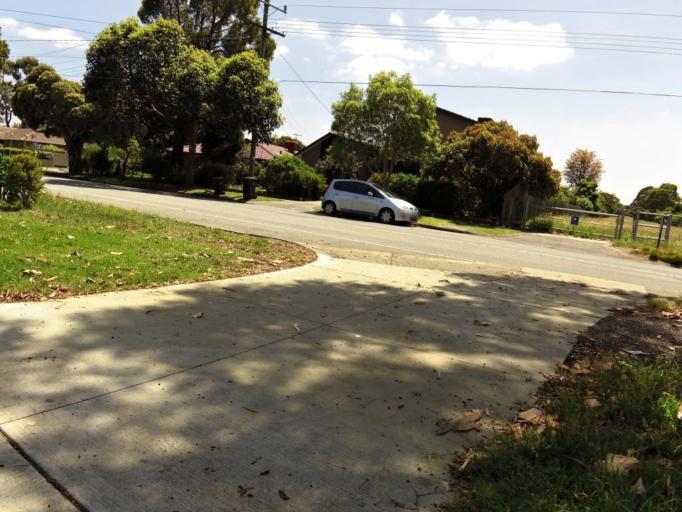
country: AU
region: Victoria
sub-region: Whitehorse
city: Vermont South
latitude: -37.8730
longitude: 145.1827
